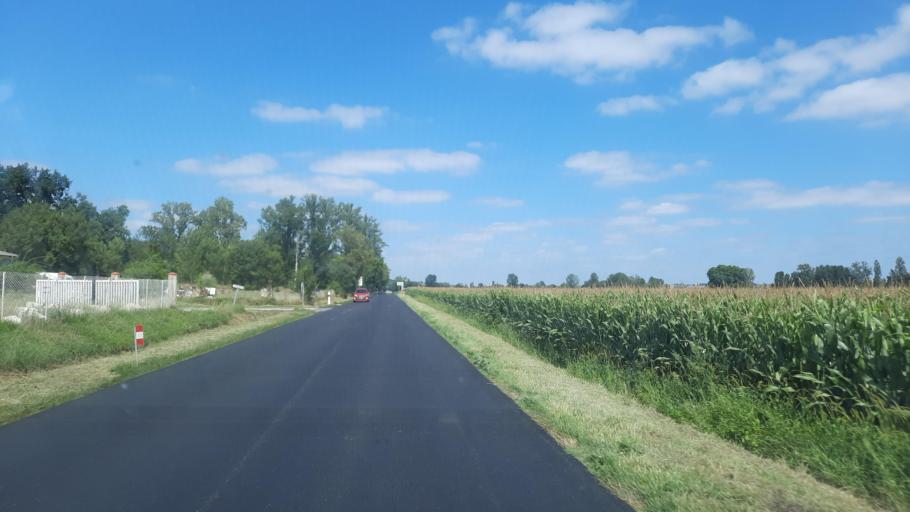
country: FR
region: Midi-Pyrenees
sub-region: Departement du Gers
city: Lombez
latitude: 43.4580
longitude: 0.8822
